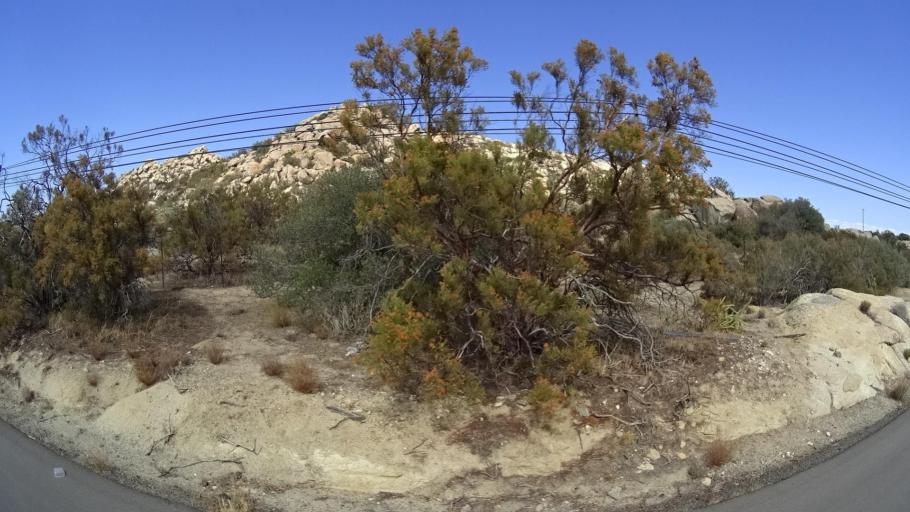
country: MX
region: Baja California
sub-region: Tecate
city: Cereso del Hongo
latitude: 32.6458
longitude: -116.2370
